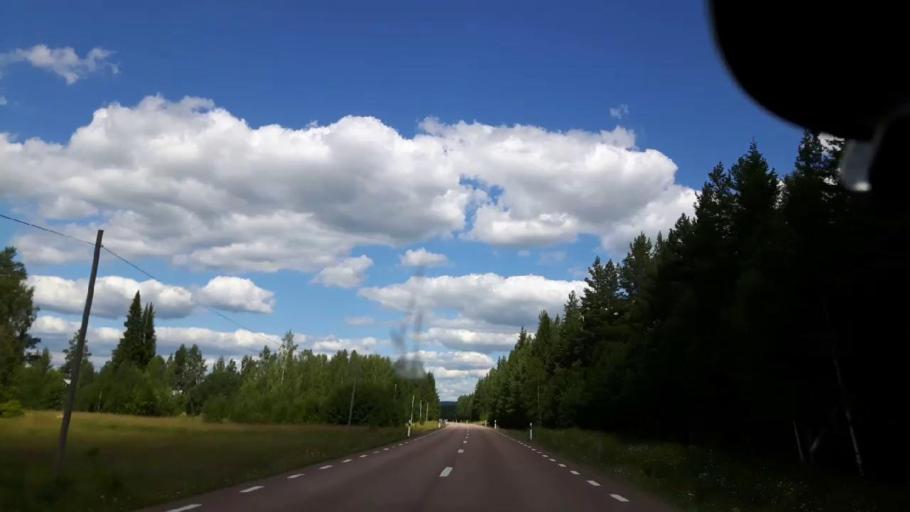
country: SE
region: Jaemtland
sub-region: Ragunda Kommun
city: Hammarstrand
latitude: 62.9076
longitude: 16.7019
